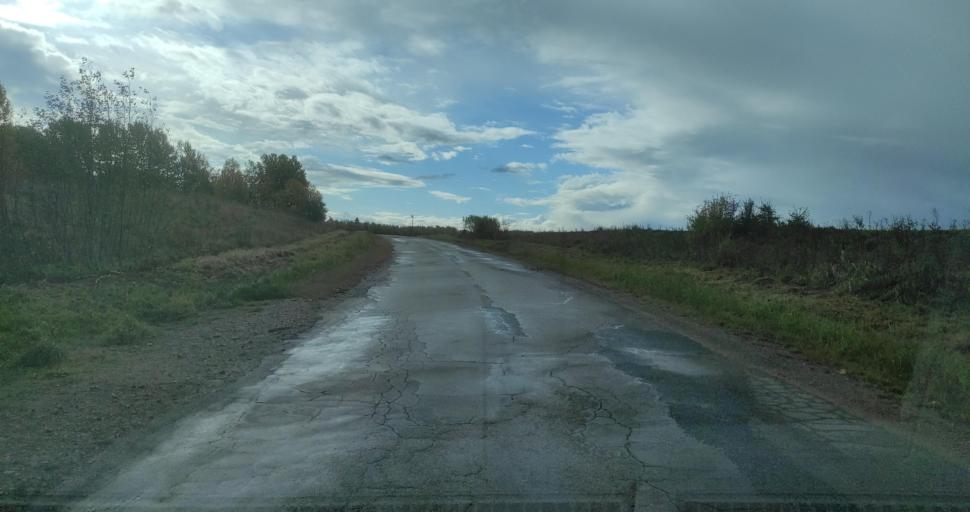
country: LV
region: Vainode
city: Vainode
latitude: 56.5606
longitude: 21.9063
